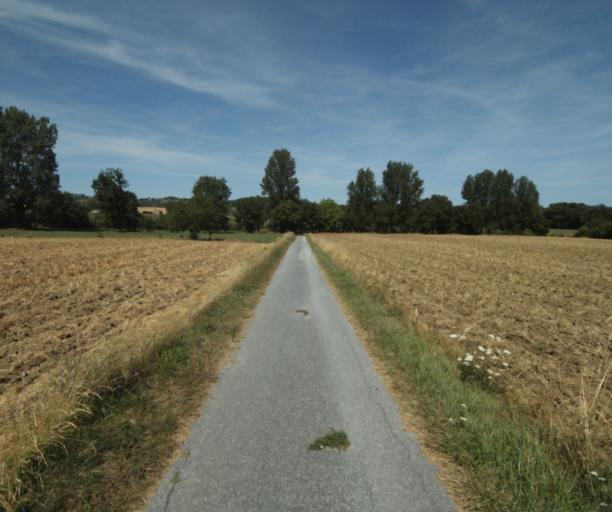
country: FR
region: Midi-Pyrenees
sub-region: Departement du Tarn
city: Puylaurens
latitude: 43.5392
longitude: 2.0195
